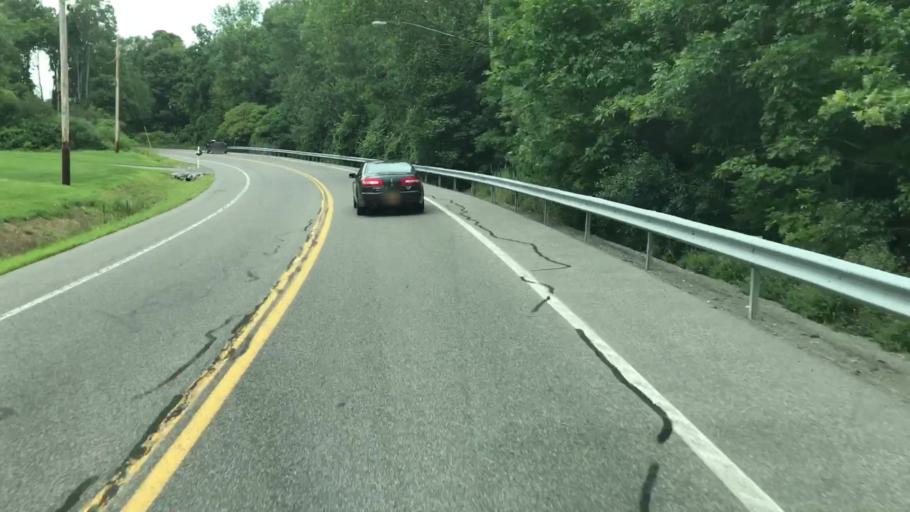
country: US
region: New York
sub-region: Onondaga County
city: Camillus
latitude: 43.0722
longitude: -76.3258
